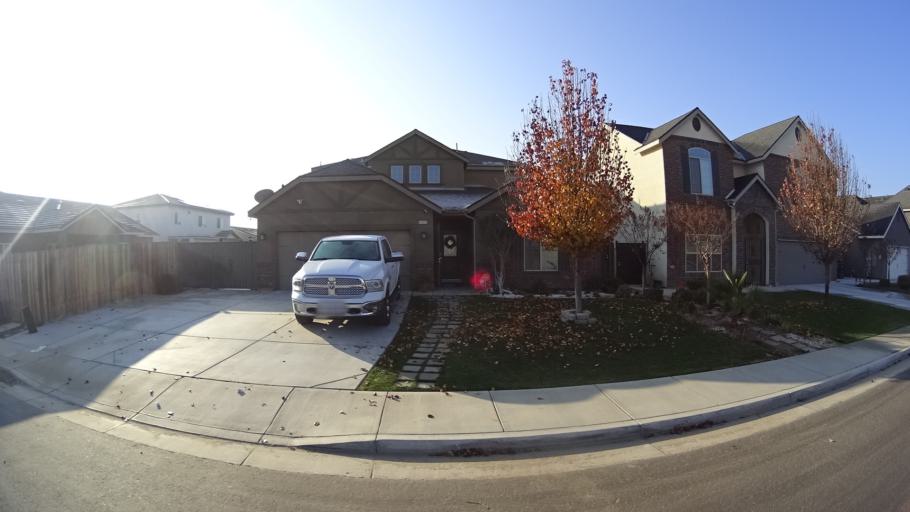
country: US
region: California
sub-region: Kern County
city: Greenacres
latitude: 35.2912
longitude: -119.1145
